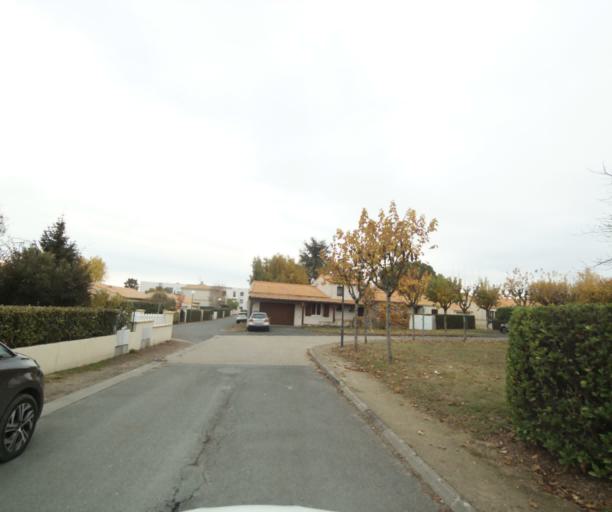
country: FR
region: Poitou-Charentes
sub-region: Departement de la Charente-Maritime
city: Saintes
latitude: 45.7445
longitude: -0.6583
